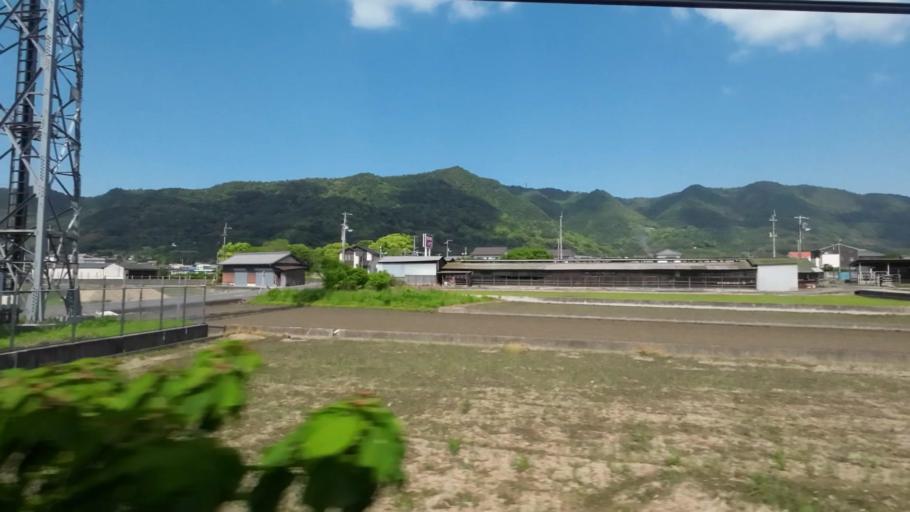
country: JP
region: Kagawa
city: Kan'onjicho
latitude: 34.1573
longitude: 133.6885
